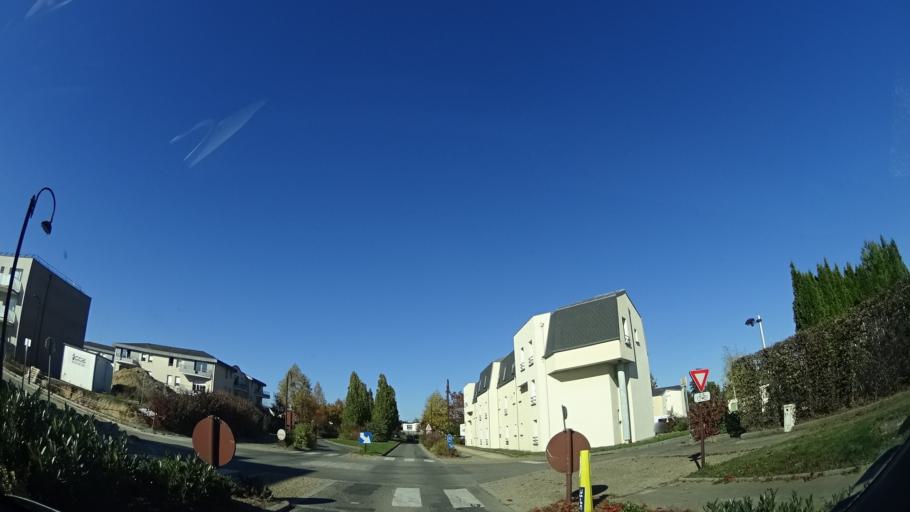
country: FR
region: Brittany
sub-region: Departement d'Ille-et-Vilaine
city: La Meziere
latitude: 48.2132
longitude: -1.7547
